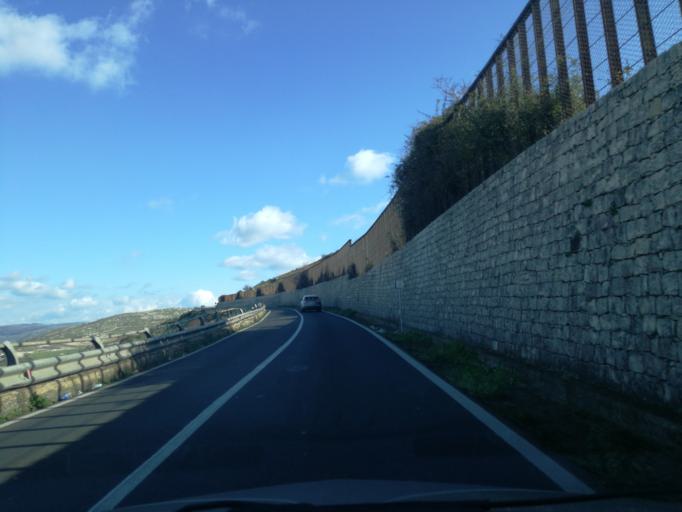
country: IT
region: Sicily
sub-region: Ragusa
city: Comiso
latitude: 36.9389
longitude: 14.6284
